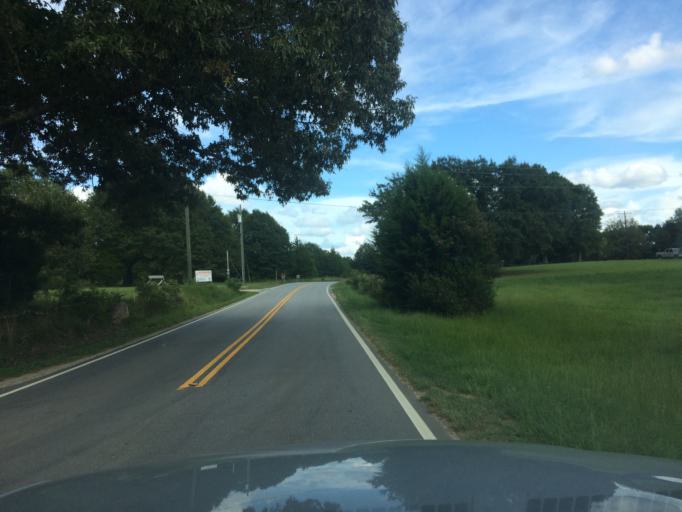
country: US
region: South Carolina
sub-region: Greenville County
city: Fountain Inn
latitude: 34.7432
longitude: -82.1305
